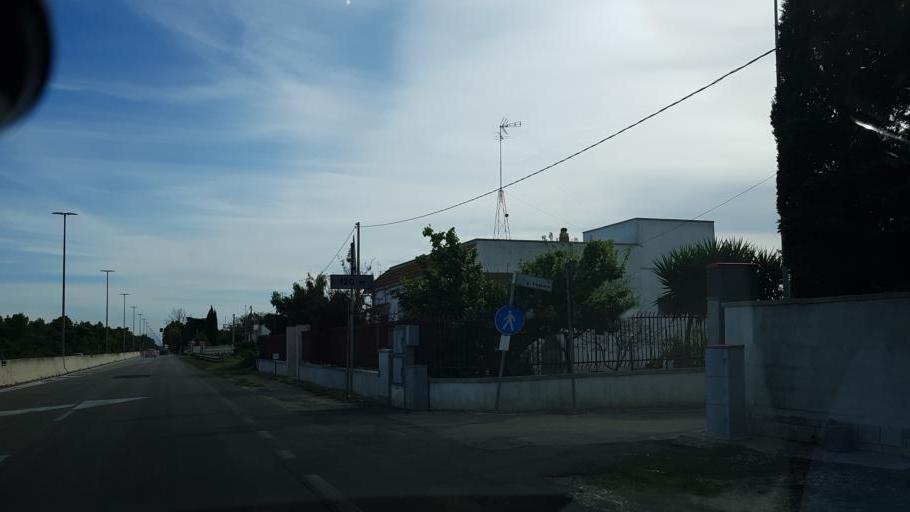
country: IT
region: Apulia
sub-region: Provincia di Lecce
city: Struda
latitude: 40.3849
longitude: 18.2868
